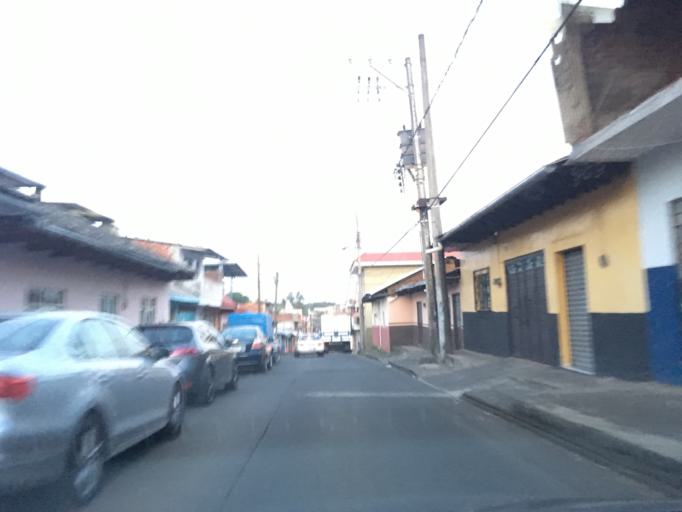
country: MX
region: Michoacan
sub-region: Uruapan
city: Uruapan
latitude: 19.4125
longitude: -102.0642
